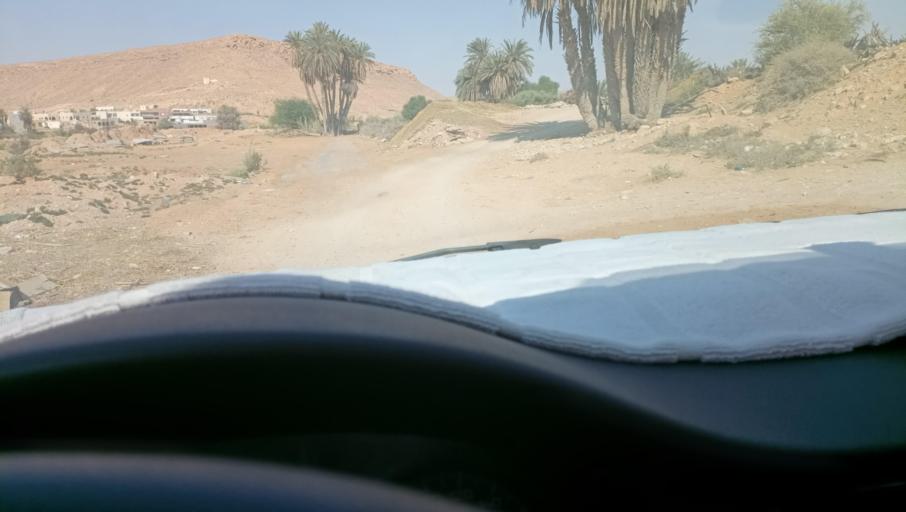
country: TN
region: Tataouine
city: Tataouine
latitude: 32.9807
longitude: 10.3828
